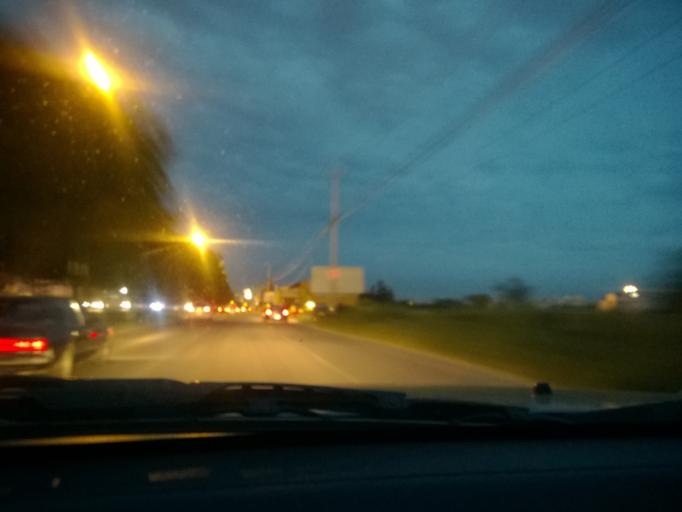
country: MX
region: Guanajuato
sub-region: Leon
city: Medina
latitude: 21.1274
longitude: -101.6413
